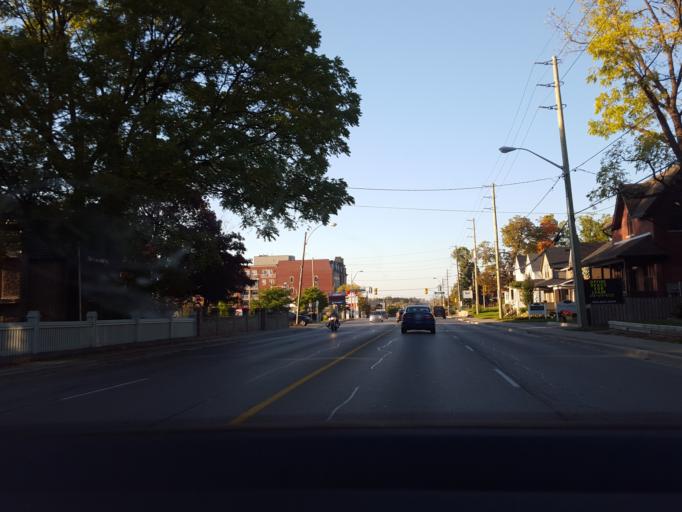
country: CA
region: Ontario
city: Newmarket
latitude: 44.0028
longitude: -79.4683
